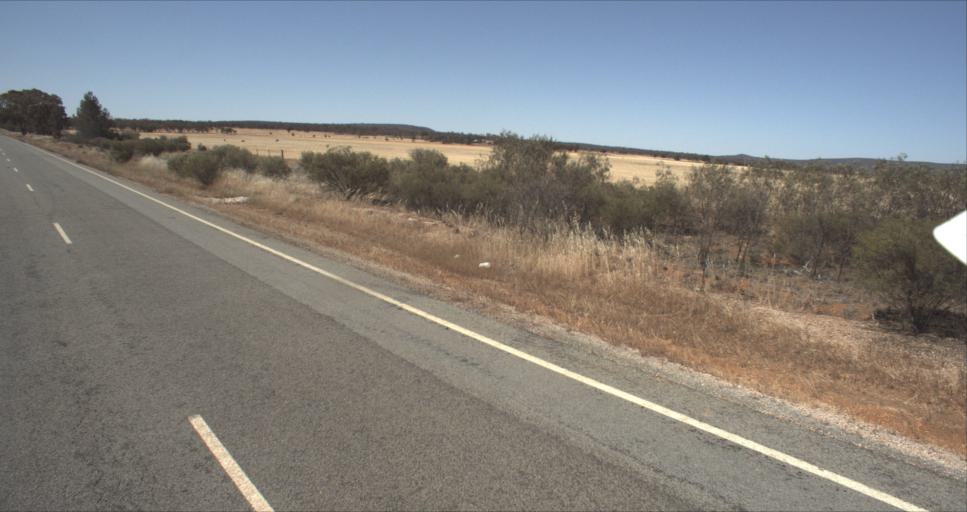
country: AU
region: New South Wales
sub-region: Leeton
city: Leeton
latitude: -34.4909
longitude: 146.4324
